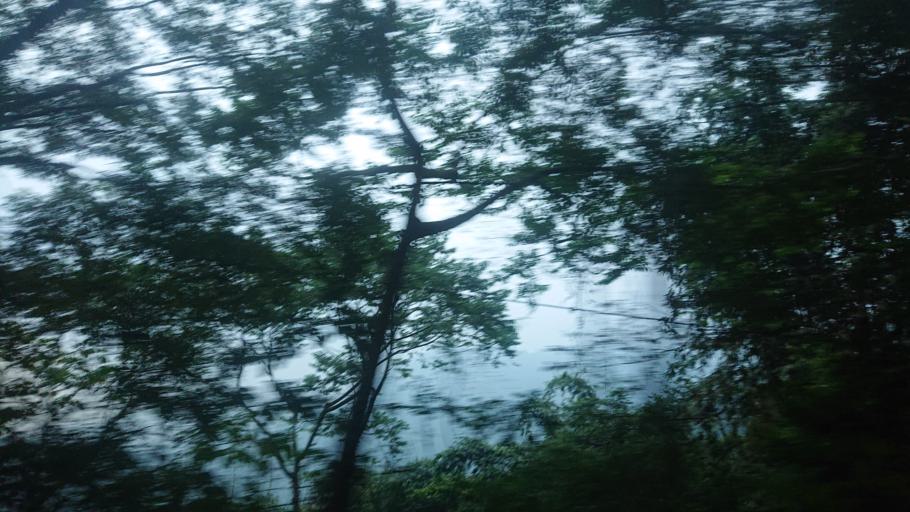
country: TW
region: Taiwan
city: Lugu
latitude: 23.5870
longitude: 120.7267
